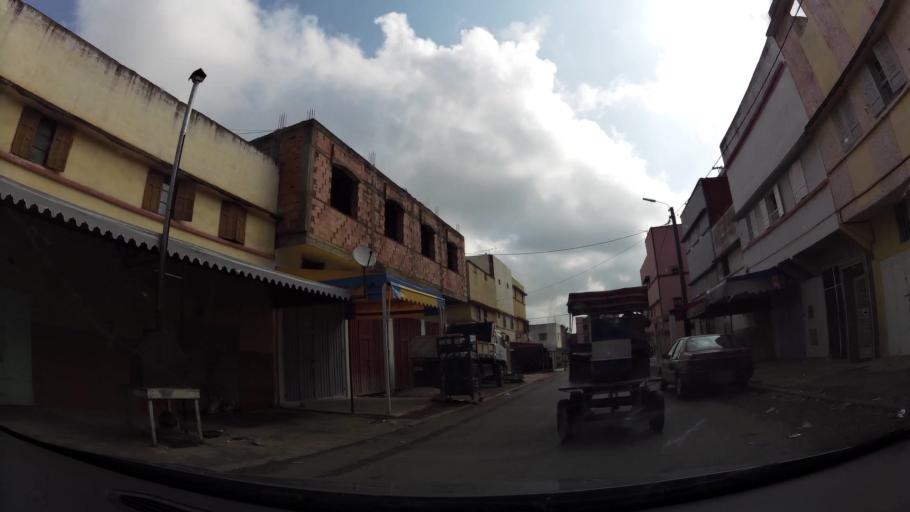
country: MA
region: Rabat-Sale-Zemmour-Zaer
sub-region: Khemisset
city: Tiflet
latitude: 33.8879
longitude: -6.3125
